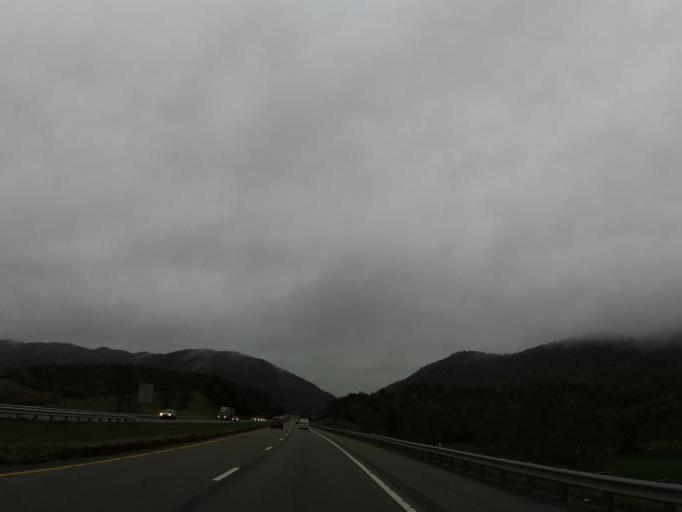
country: US
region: Virginia
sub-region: Wythe County
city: Wytheville
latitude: 37.0040
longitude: -81.0967
